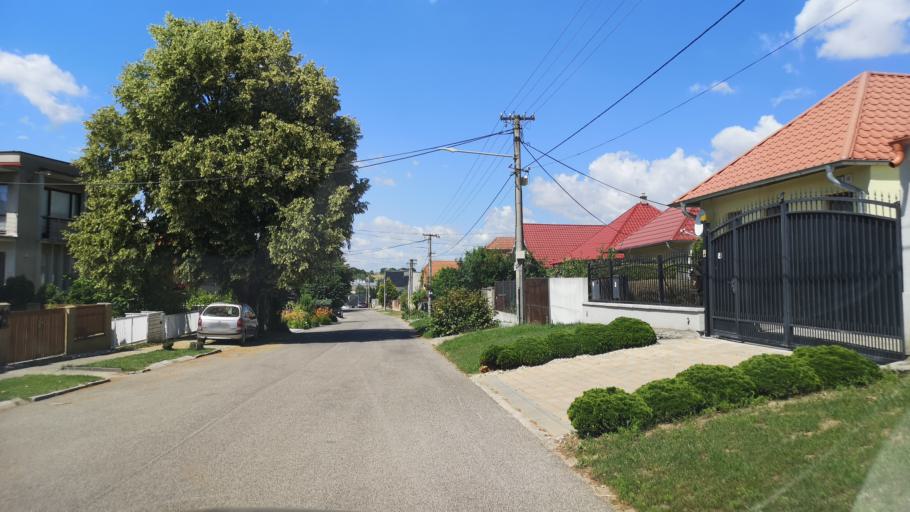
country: SK
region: Nitriansky
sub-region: Okres Nitra
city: Nitra
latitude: 48.2787
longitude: 17.9505
